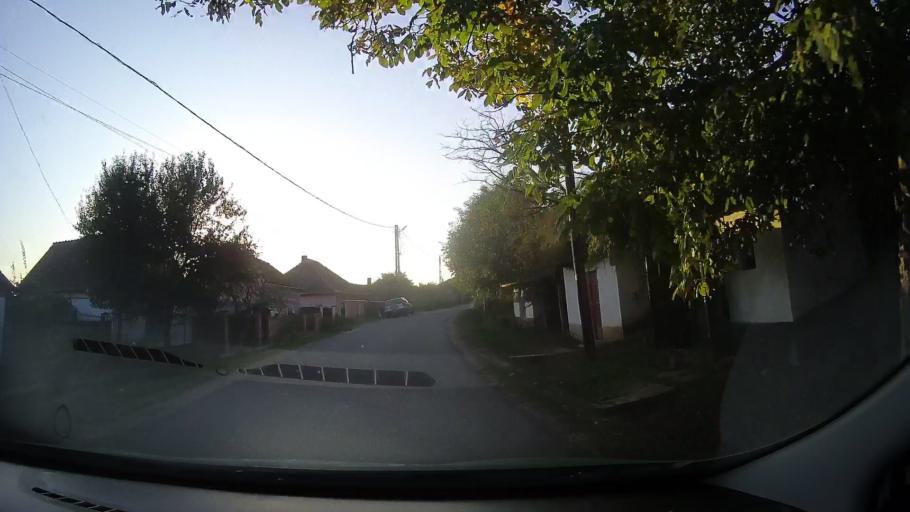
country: RO
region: Bihor
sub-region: Comuna Rosiori
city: Rosiori
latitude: 47.2499
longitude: 22.0018
